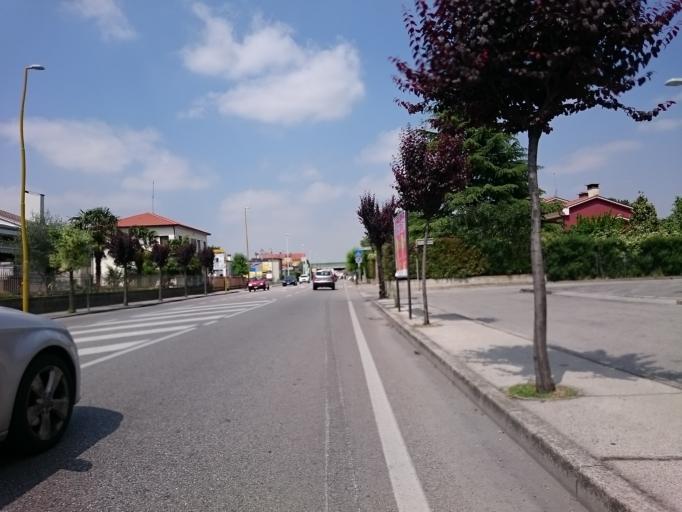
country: IT
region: Veneto
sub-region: Provincia di Padova
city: Ponte San Nicolo
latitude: 45.3736
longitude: 11.9134
